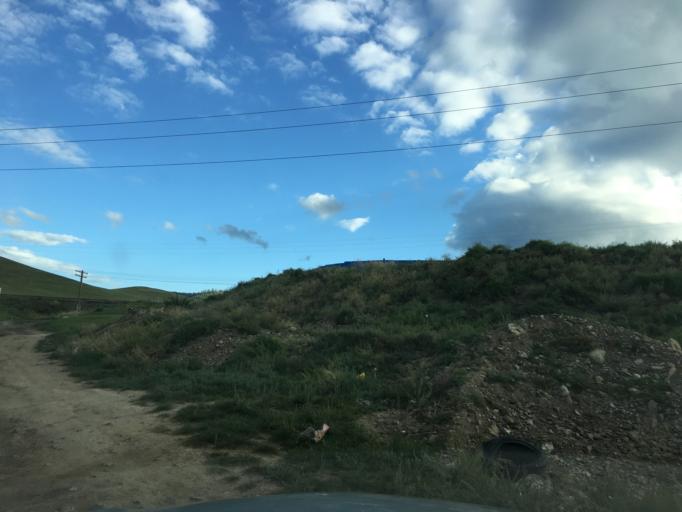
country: MN
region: Ulaanbaatar
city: Ulaanbaatar
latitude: 47.8873
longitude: 107.0596
